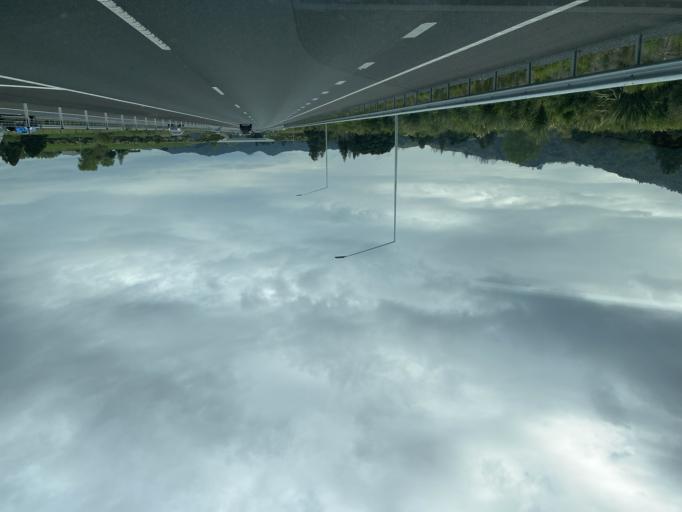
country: NZ
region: Waikato
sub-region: Waikato District
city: Ngaruawahia
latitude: -37.6165
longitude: 175.2048
